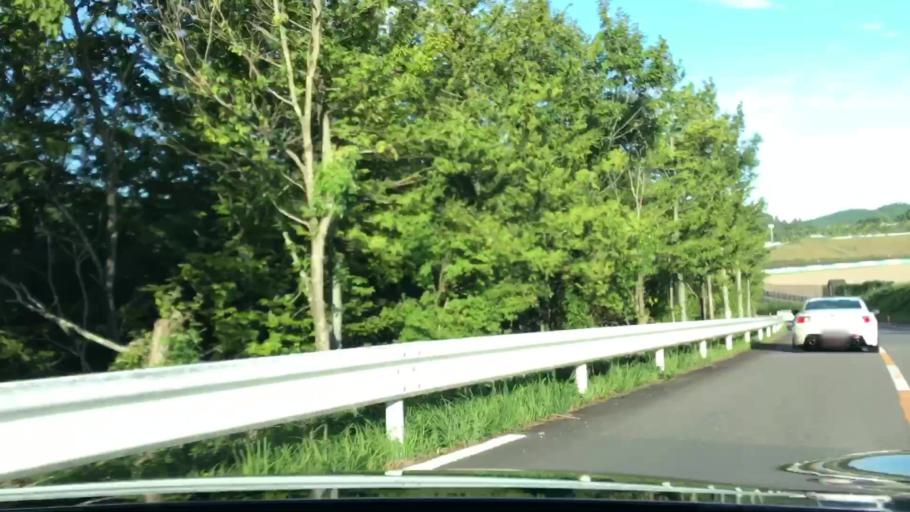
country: JP
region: Tochigi
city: Motegi
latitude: 36.5372
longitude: 140.2283
